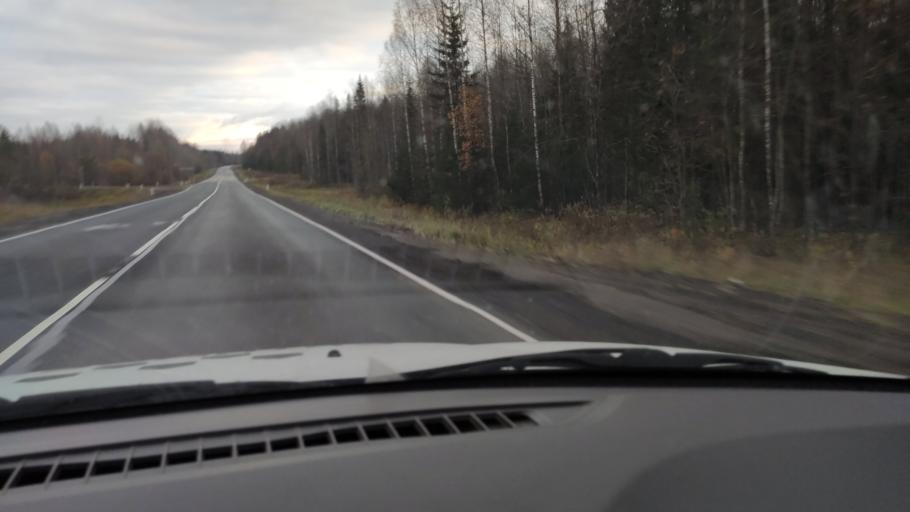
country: RU
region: Kirov
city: Omutninsk
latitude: 58.7563
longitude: 52.0336
